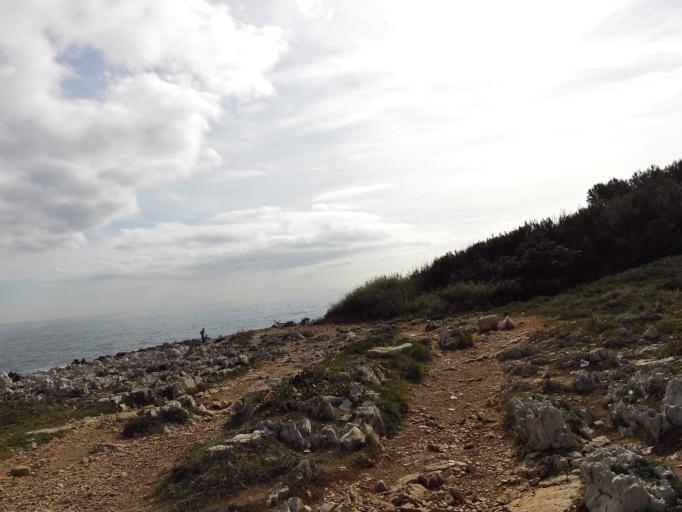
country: FR
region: Provence-Alpes-Cote d'Azur
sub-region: Departement des Alpes-Maritimes
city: Antibes
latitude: 43.5474
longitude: 7.1379
